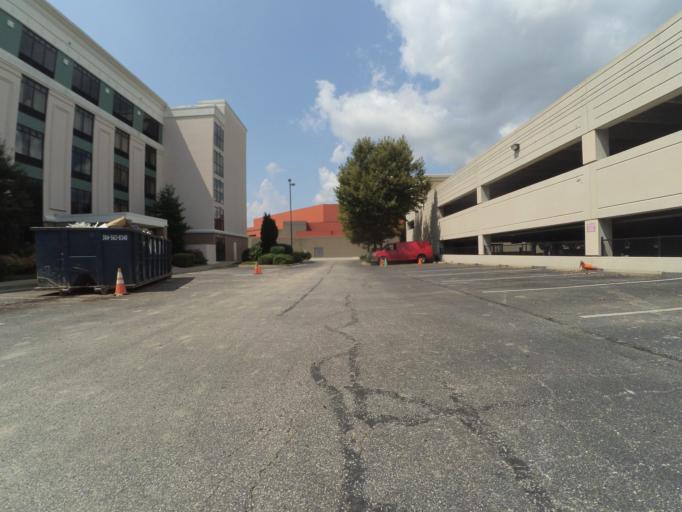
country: US
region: West Virginia
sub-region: Cabell County
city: Huntington
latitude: 38.4225
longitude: -82.4452
